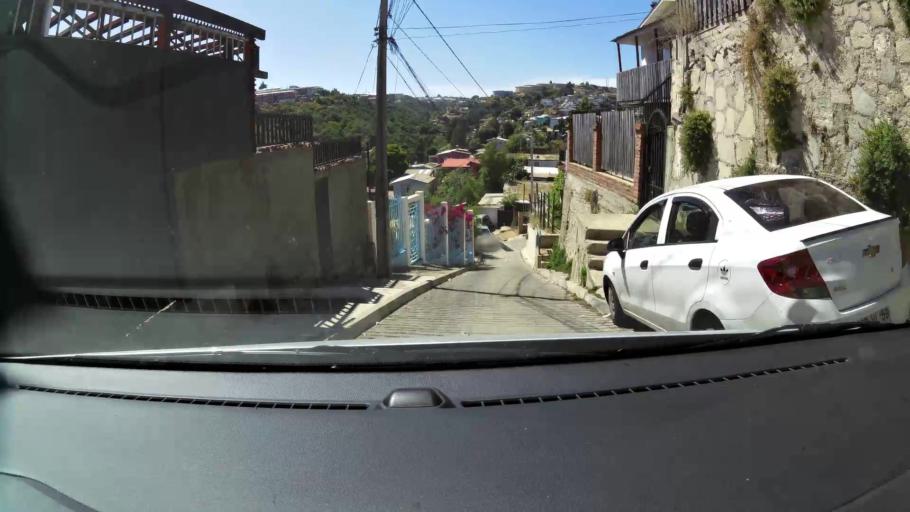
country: CL
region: Valparaiso
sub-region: Provincia de Valparaiso
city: Vina del Mar
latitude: -33.0536
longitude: -71.5774
